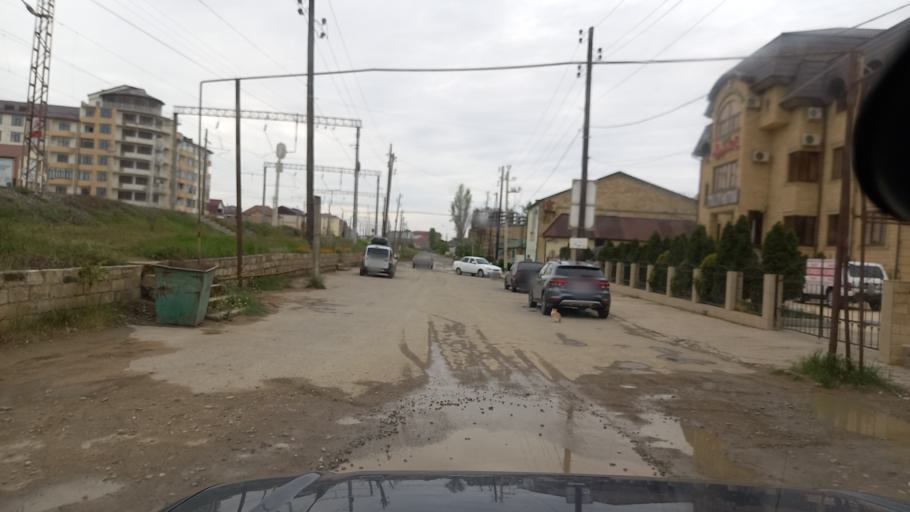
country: RU
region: Dagestan
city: Derbent
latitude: 42.0653
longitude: 48.3037
